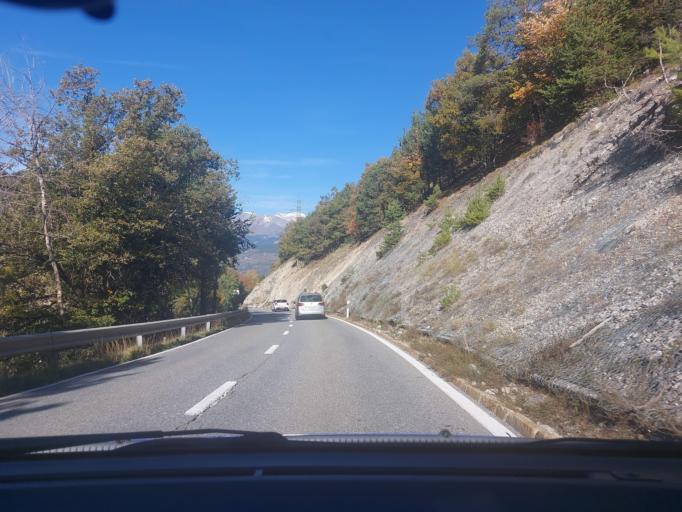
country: CH
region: Valais
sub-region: Sierre District
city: Chippis
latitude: 46.2579
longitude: 7.5693
